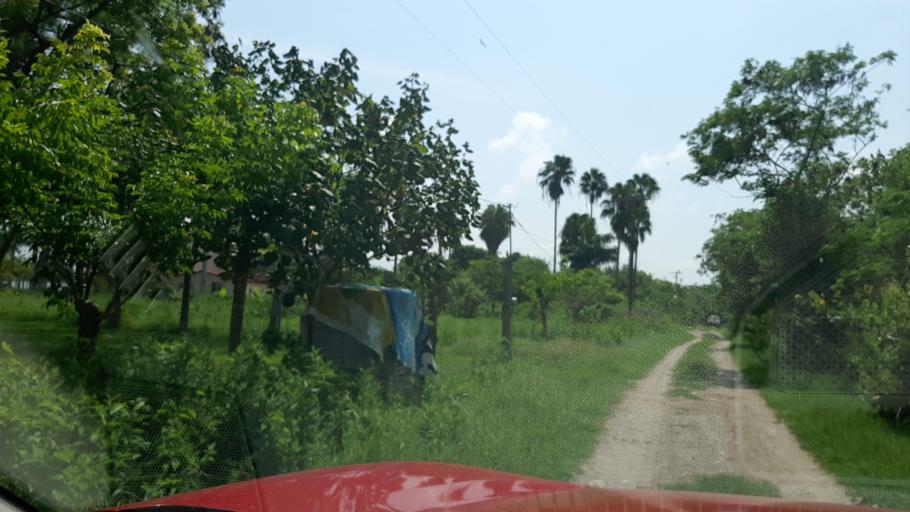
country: MX
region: Veracruz
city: Nautla
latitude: 20.2490
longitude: -96.8018
